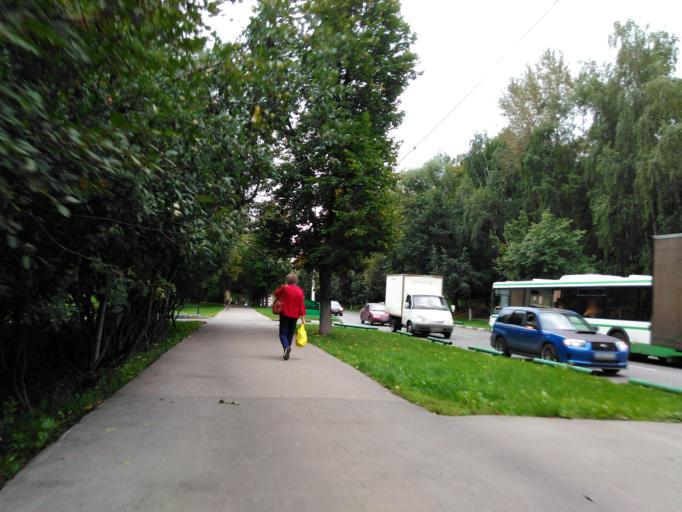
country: RU
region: Moscow
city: Zyuzino
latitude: 55.6619
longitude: 37.5850
